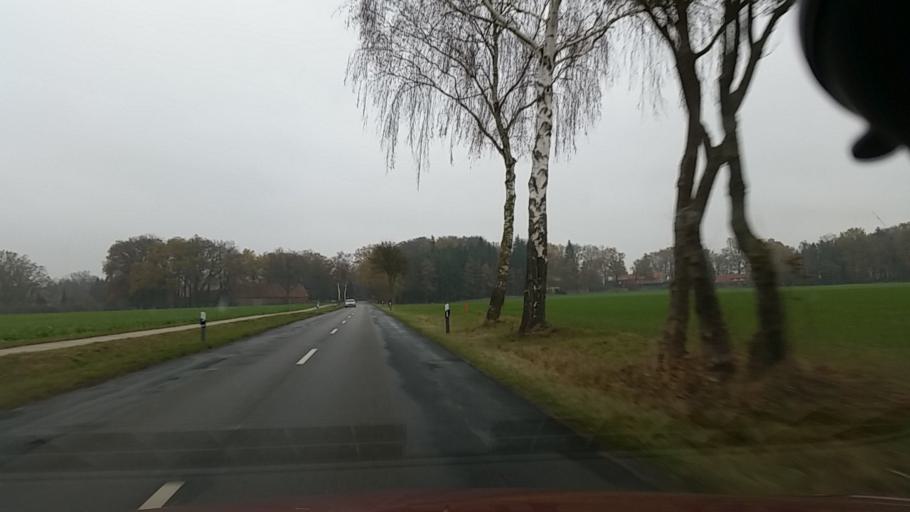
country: DE
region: Lower Saxony
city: Wrestedt
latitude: 52.9347
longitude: 10.5743
